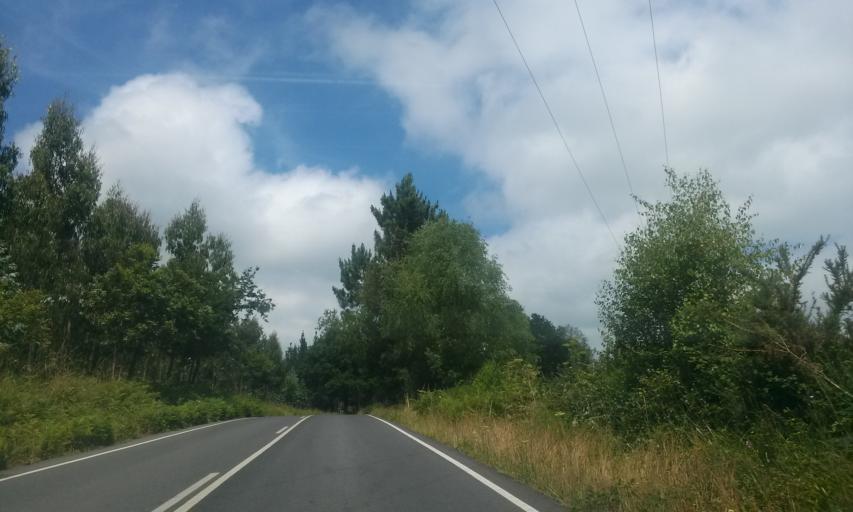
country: ES
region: Galicia
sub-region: Provincia de Lugo
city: Friol
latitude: 43.0570
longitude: -7.8370
